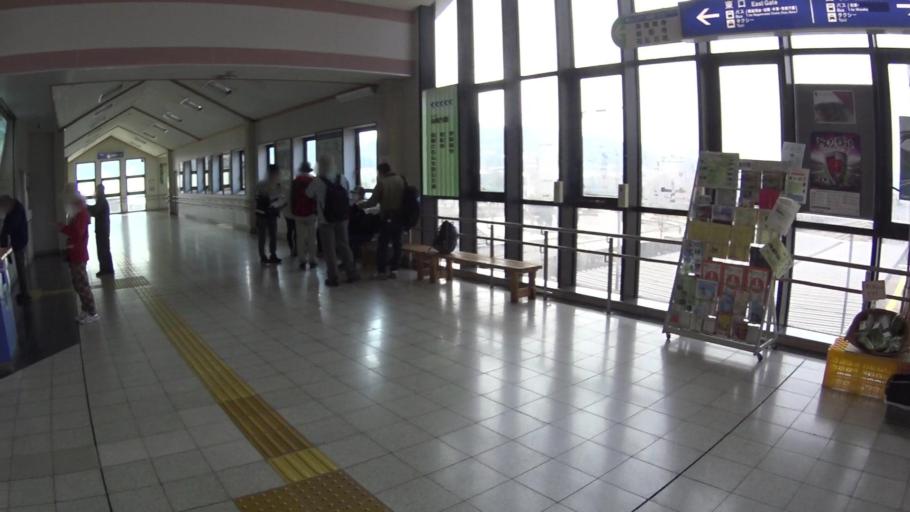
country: JP
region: Nara
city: Nara-shi
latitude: 34.7445
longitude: 135.8692
